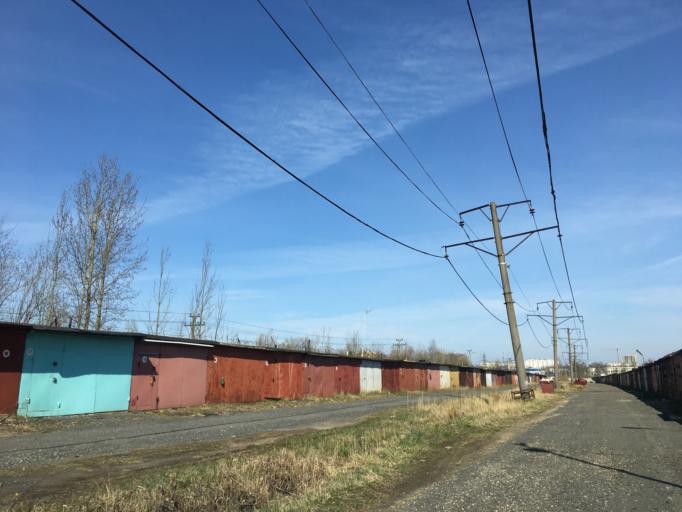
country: RU
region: St.-Petersburg
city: Uritsk
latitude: 59.8188
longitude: 30.1639
